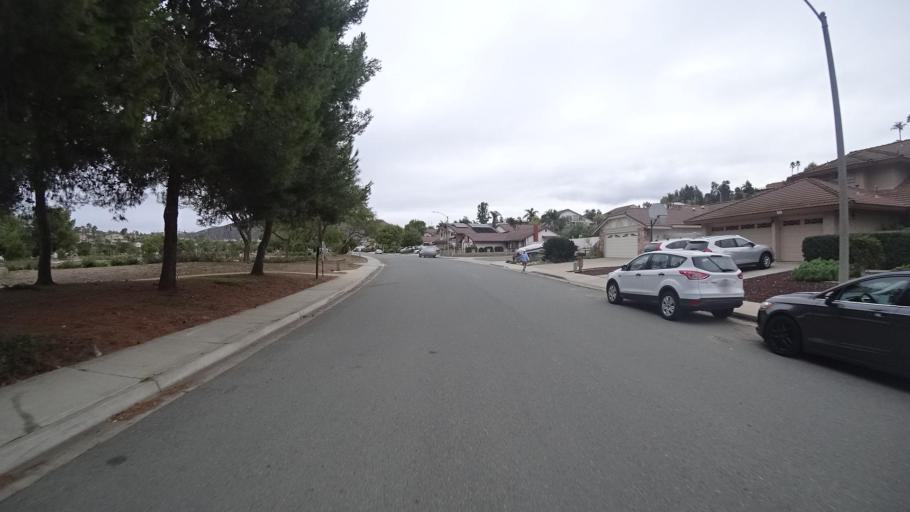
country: US
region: California
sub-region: San Diego County
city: Rancho San Diego
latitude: 32.7563
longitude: -116.9124
